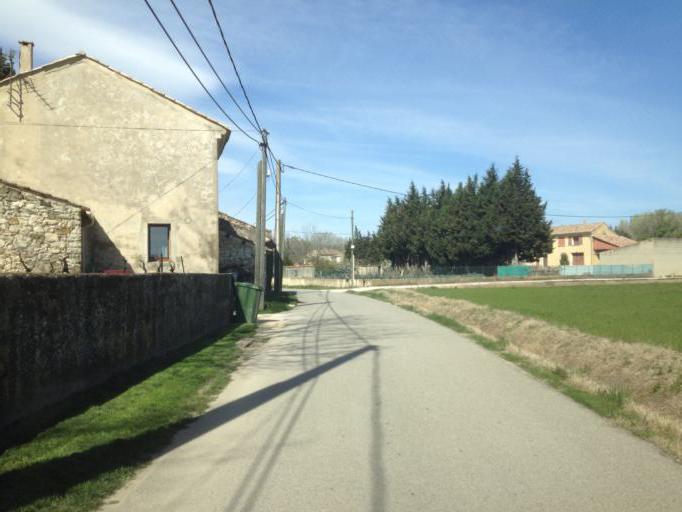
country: FR
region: Provence-Alpes-Cote d'Azur
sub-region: Departement du Vaucluse
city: Caderousse
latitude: 44.1023
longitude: 4.7335
